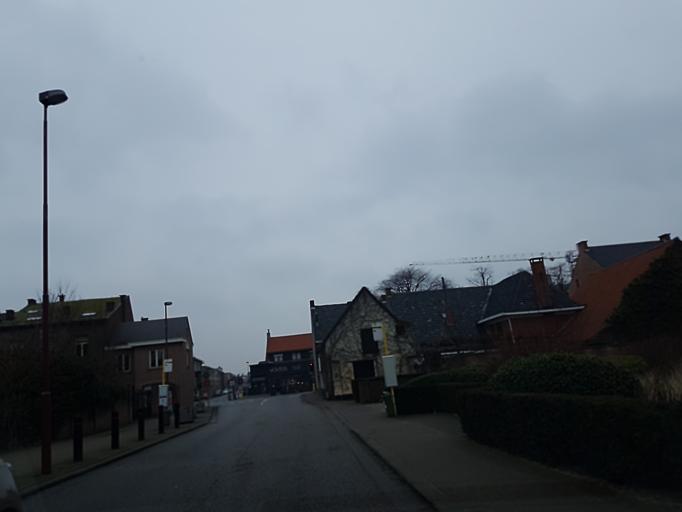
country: BE
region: Flanders
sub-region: Provincie Antwerpen
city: Stabroek
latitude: 51.3318
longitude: 4.3665
